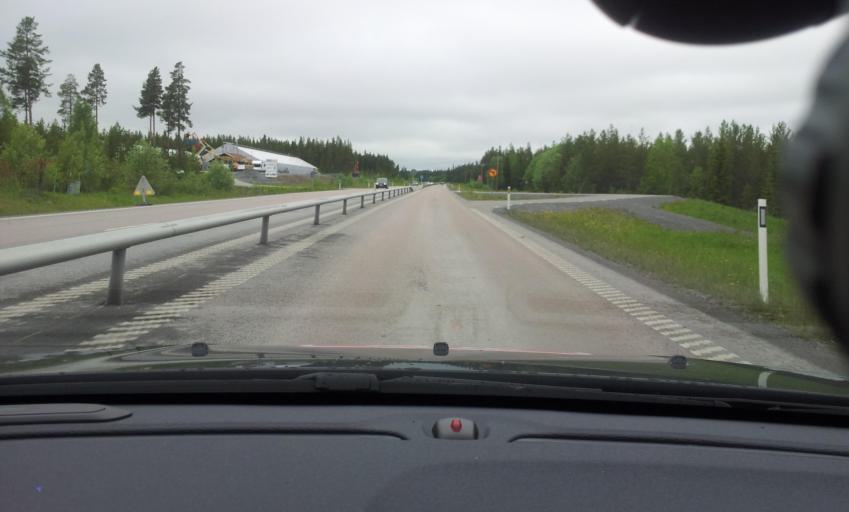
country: SE
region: Jaemtland
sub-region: OEstersunds Kommun
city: Ostersund
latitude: 63.2368
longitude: 14.6063
